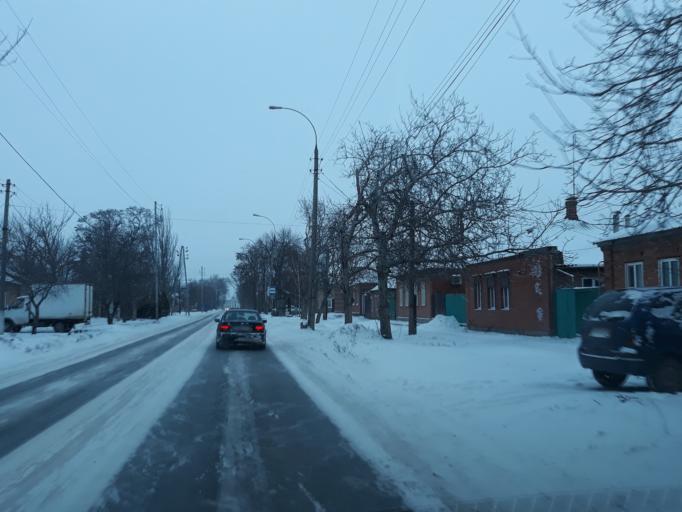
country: RU
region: Rostov
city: Taganrog
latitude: 47.2562
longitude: 38.9385
